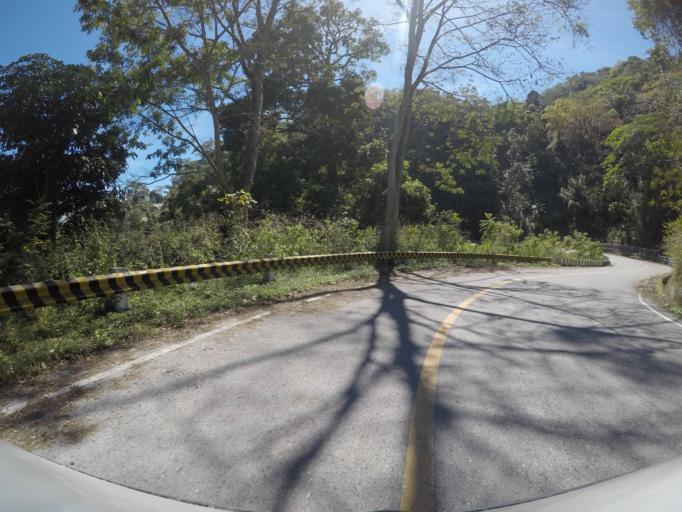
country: TL
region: Manufahi
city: Same
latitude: -8.9030
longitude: 125.9768
